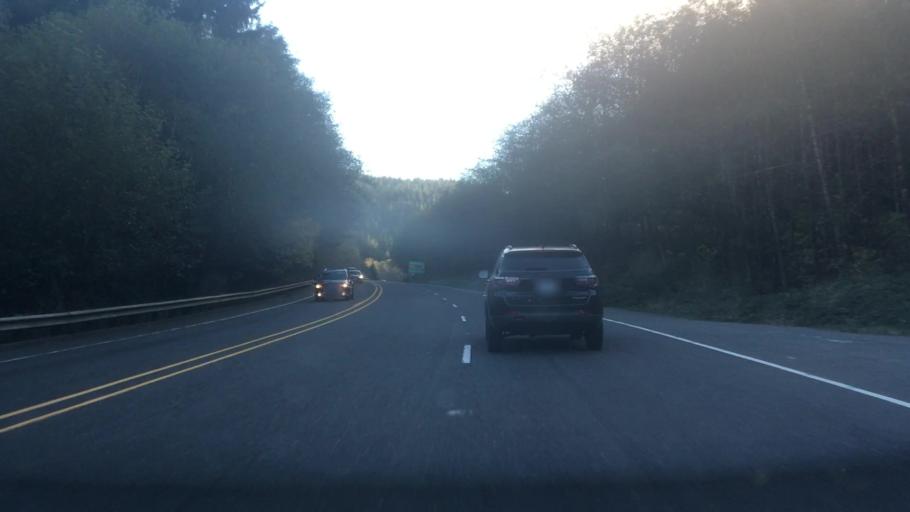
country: US
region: Oregon
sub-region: Clatsop County
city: Cannon Beach
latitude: 45.9190
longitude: -123.9381
